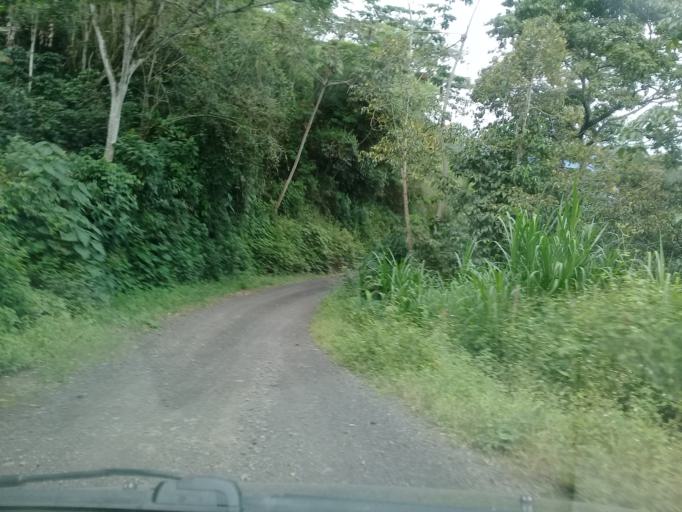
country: CO
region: Cundinamarca
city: Viani
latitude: 4.8476
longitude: -74.5474
